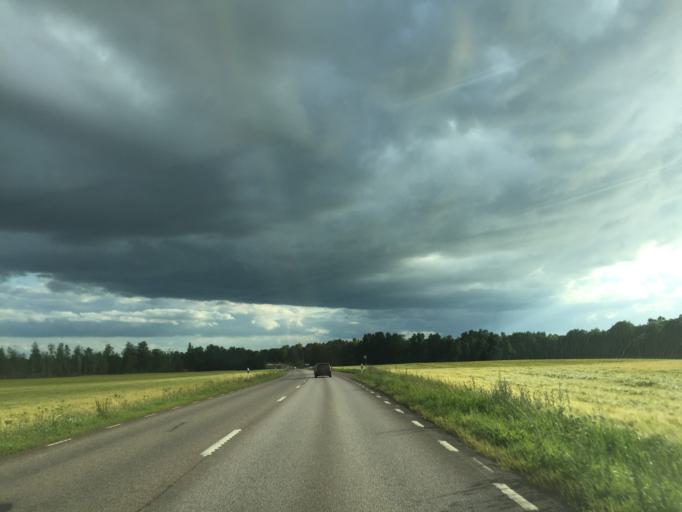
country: SE
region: OEstergoetland
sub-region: Vadstena Kommun
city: Vadstena
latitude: 58.4737
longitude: 14.9476
